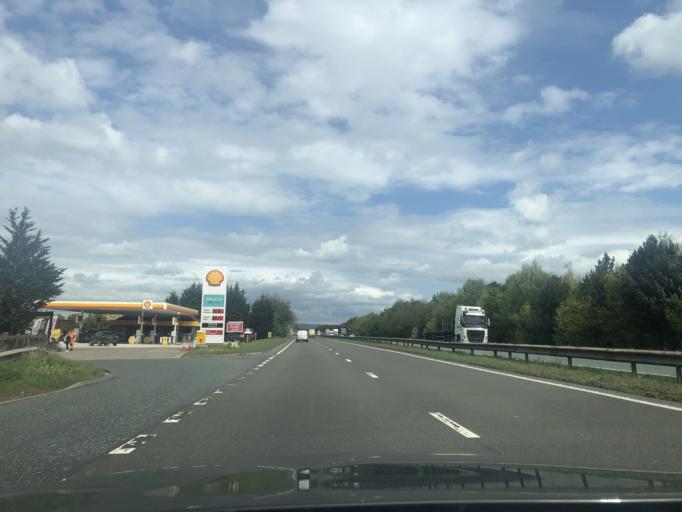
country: GB
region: England
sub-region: North Yorkshire
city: Thirsk
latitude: 54.1968
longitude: -1.3628
